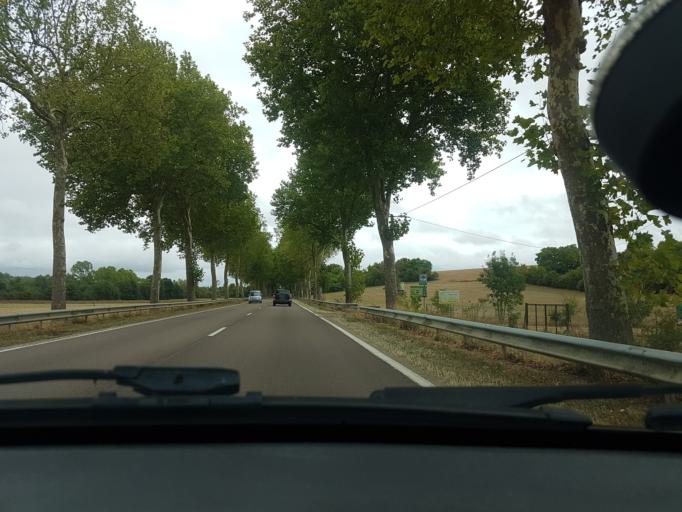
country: FR
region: Bourgogne
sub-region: Departement de l'Yonne
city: Champs-sur-Yonne
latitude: 47.7155
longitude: 3.6178
